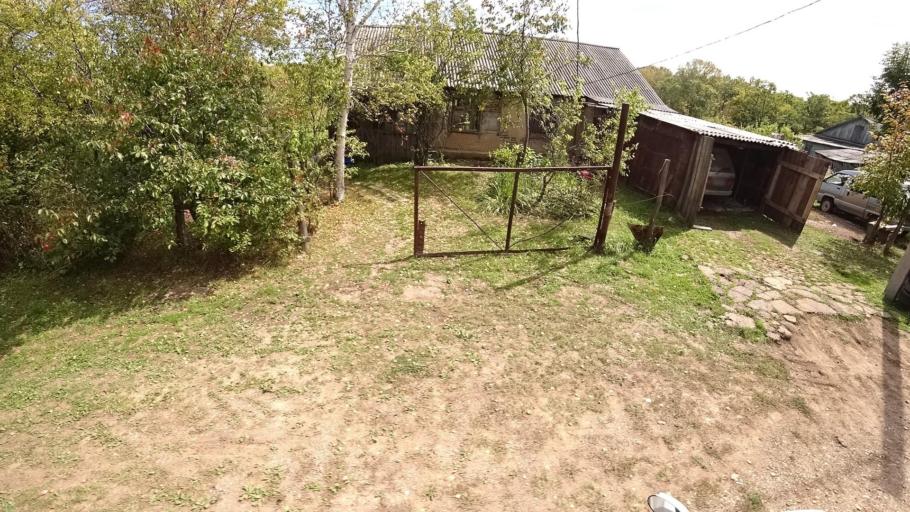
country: RU
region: Primorskiy
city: Yakovlevka
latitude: 44.7088
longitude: 133.6290
